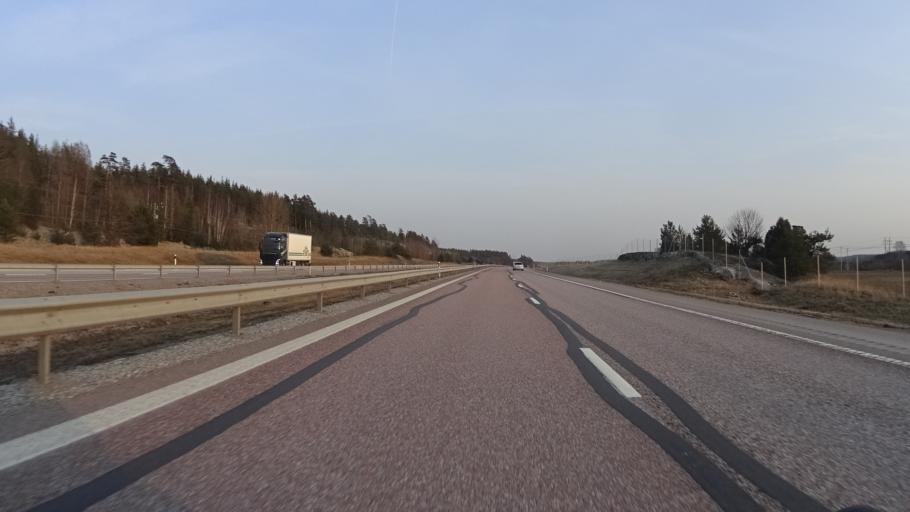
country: SE
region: Soedermanland
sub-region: Strangnas Kommun
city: Akers Styckebruk
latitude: 59.2650
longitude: 17.1409
